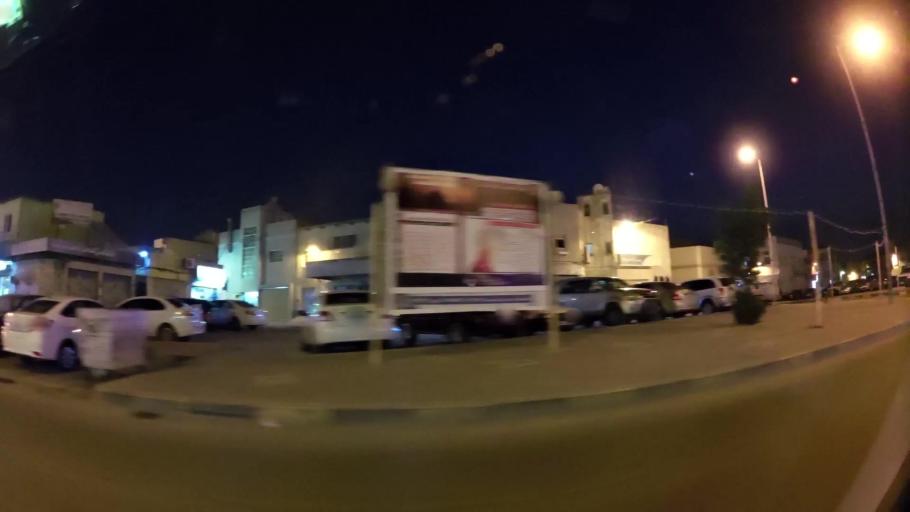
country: BH
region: Manama
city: Jidd Hafs
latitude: 26.2126
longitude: 50.5421
